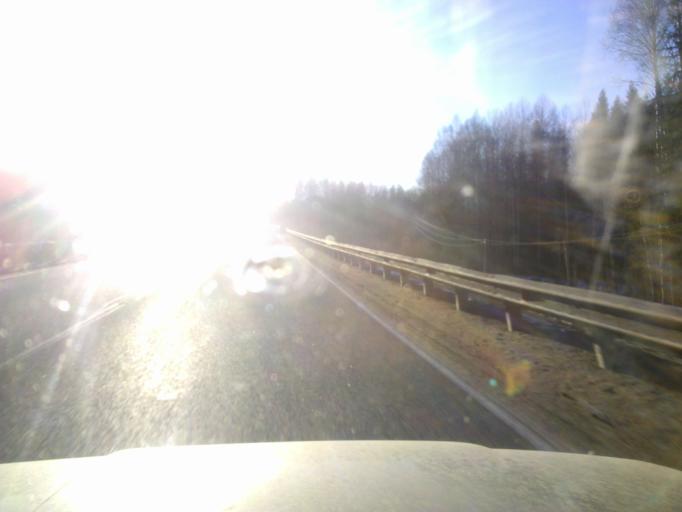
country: RU
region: Republic of Karelia
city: Girvas
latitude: 62.5043
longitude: 33.8705
